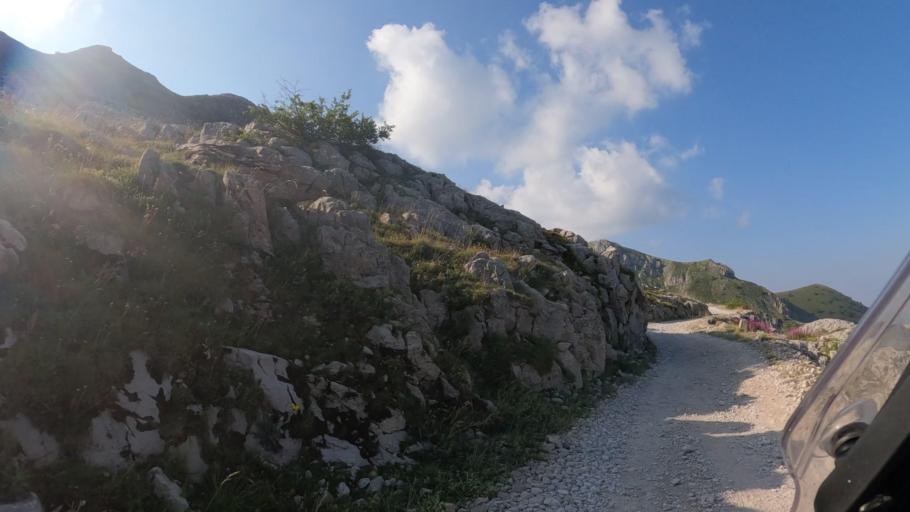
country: IT
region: Piedmont
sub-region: Provincia di Cuneo
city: Limone Piemonte
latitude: 44.1638
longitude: 7.6697
